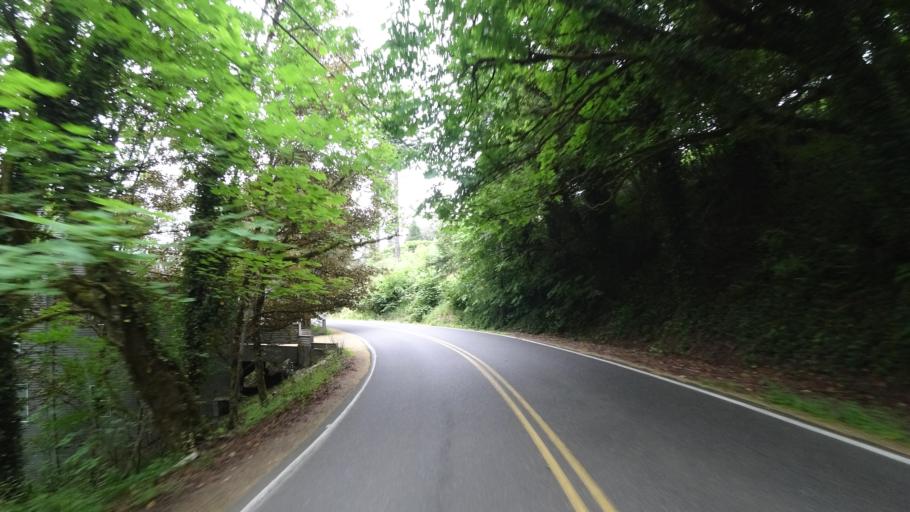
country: US
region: Oregon
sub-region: Multnomah County
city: Portland
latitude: 45.4888
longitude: -122.6945
